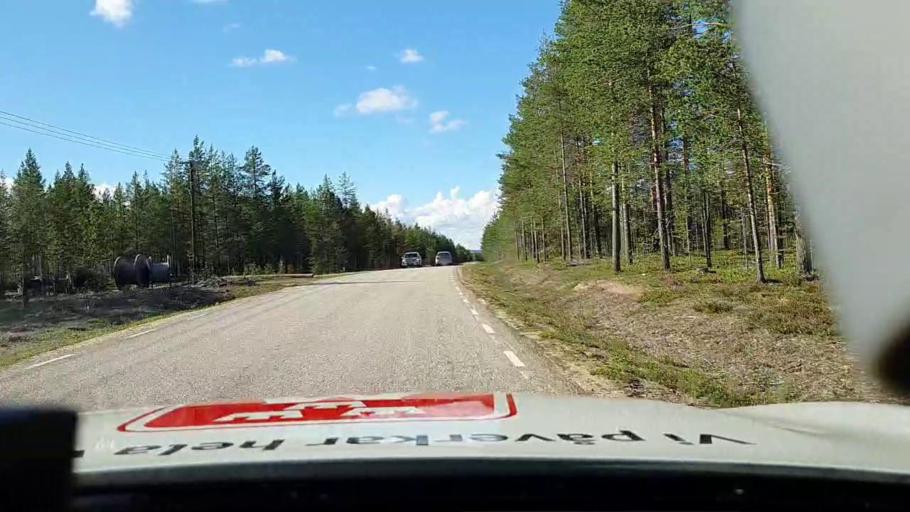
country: SE
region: Norrbotten
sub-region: Overkalix Kommun
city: OEverkalix
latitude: 66.2381
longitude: 22.9318
